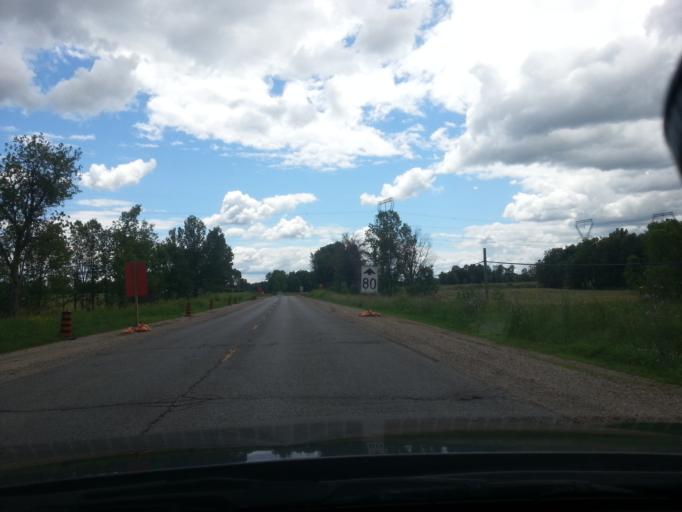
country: CA
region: Ontario
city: Gananoque
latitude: 44.5986
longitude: -76.2112
